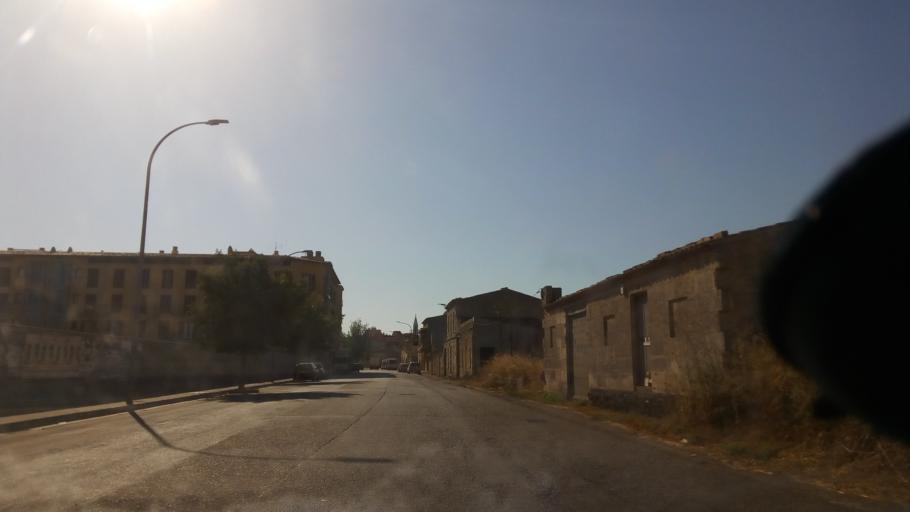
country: ES
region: Balearic Islands
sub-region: Illes Balears
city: Manacor
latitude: 39.5717
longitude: 3.1974
